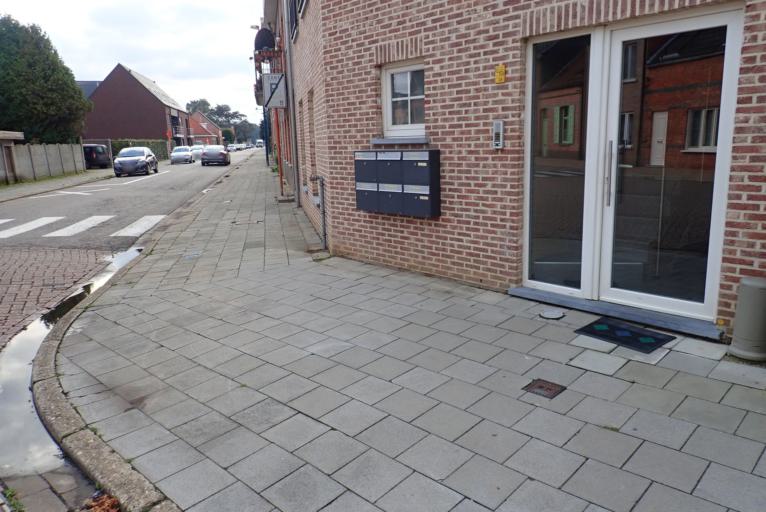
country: BE
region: Flanders
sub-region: Provincie Antwerpen
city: Vorselaar
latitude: 51.2044
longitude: 4.7692
